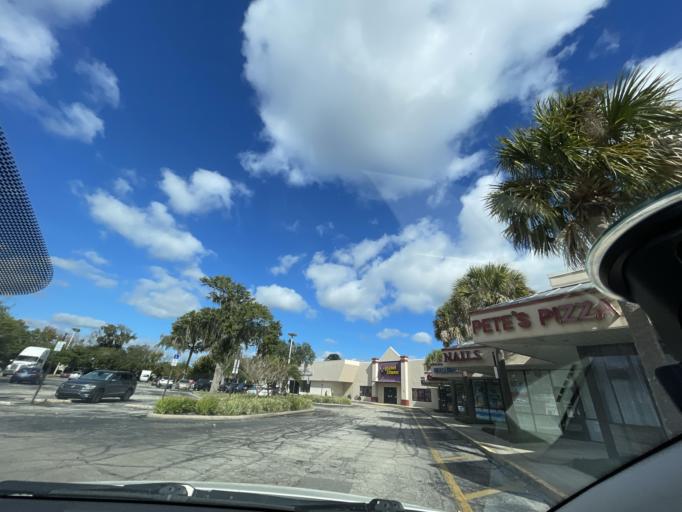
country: US
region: Florida
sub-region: Volusia County
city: South Daytona
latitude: 29.1780
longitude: -81.0273
